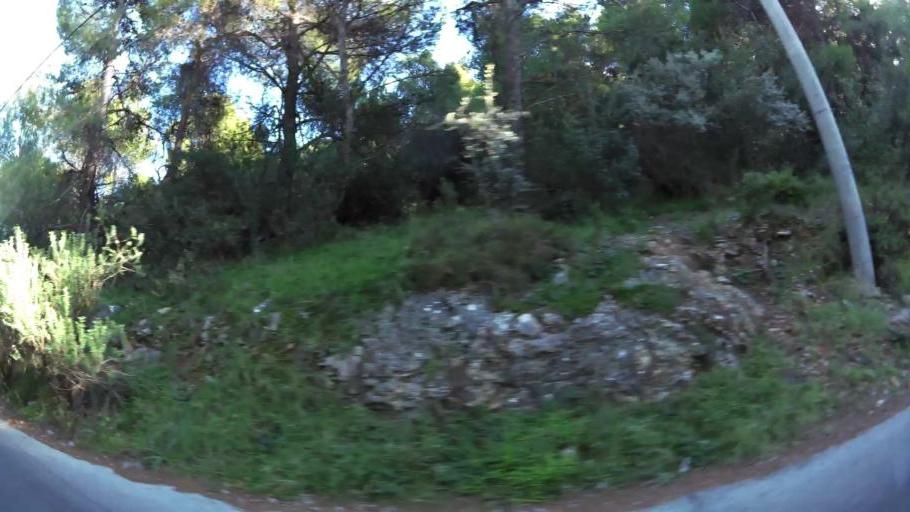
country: GR
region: Attica
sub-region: Nomarchia Athinas
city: Ekali
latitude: 38.1001
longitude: 23.8380
